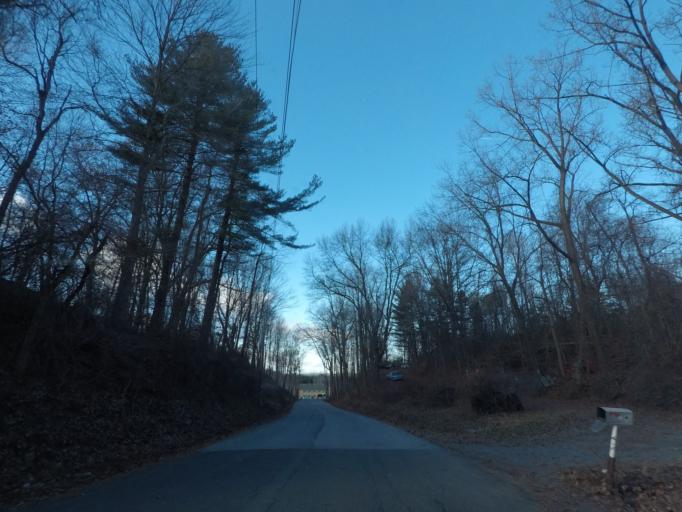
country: US
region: New York
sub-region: Saratoga County
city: Country Knolls
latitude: 42.8884
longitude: -73.7697
